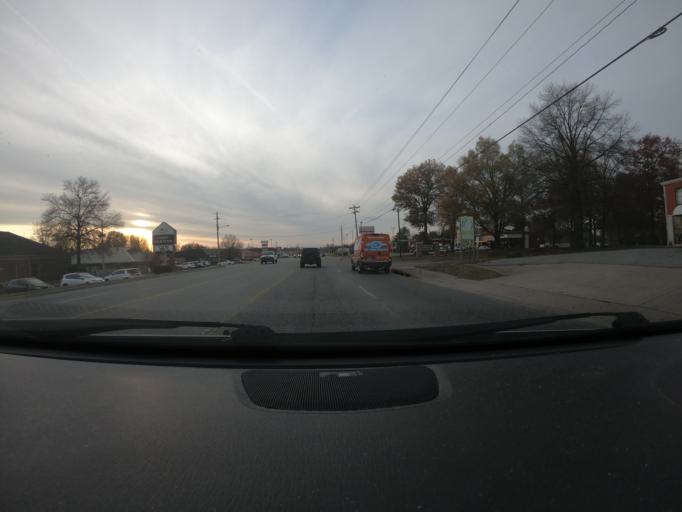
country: US
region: Arkansas
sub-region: Benton County
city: Rogers
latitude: 36.3343
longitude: -94.1546
